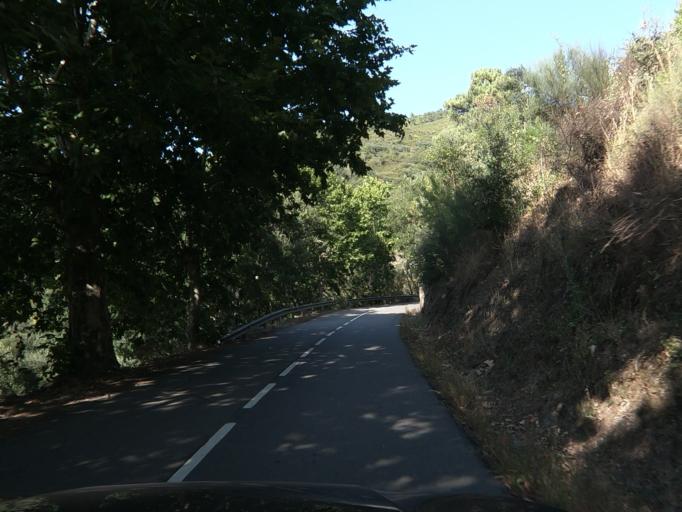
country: PT
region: Vila Real
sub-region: Sabrosa
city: Vilela
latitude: 41.2035
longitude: -7.6260
